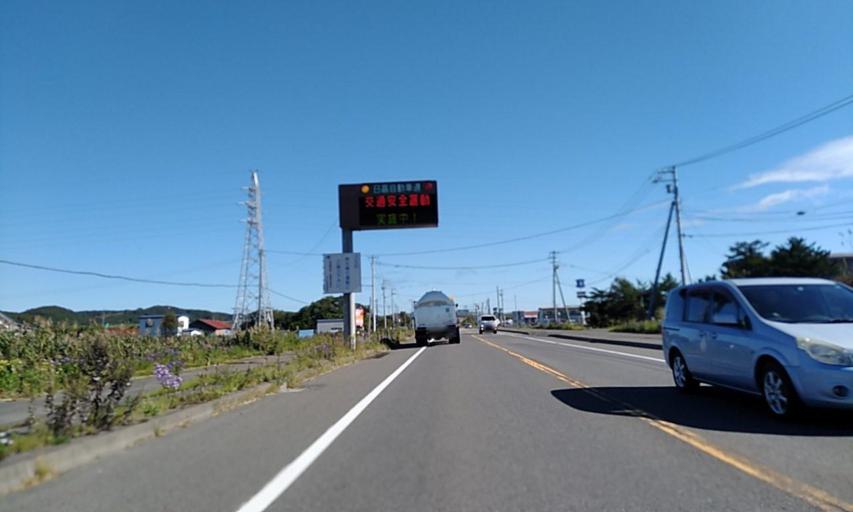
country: JP
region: Hokkaido
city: Shizunai-furukawacho
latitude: 42.5237
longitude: 142.0389
